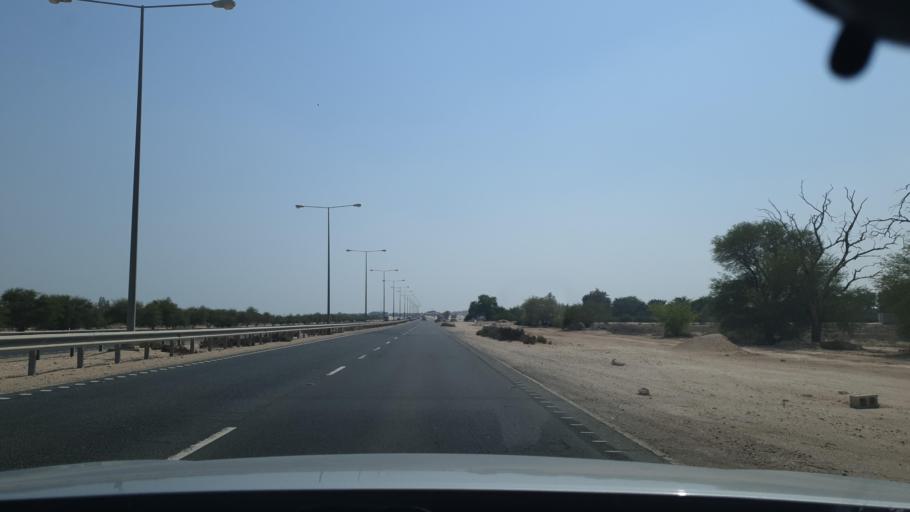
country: QA
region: Al Khawr
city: Al Khawr
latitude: 25.7315
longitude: 51.4942
